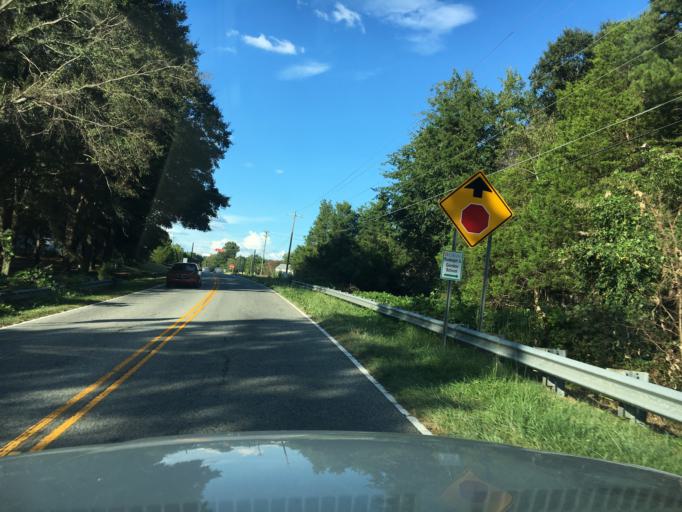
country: US
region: South Carolina
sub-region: Greenville County
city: Five Forks
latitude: 34.7605
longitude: -82.2036
